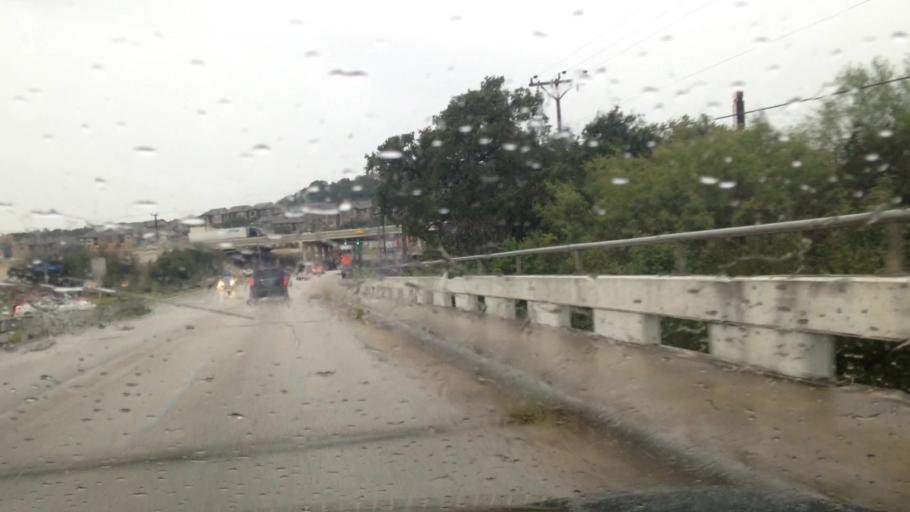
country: US
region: Texas
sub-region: Bexar County
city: Cross Mountain
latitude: 29.6265
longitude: -98.6076
